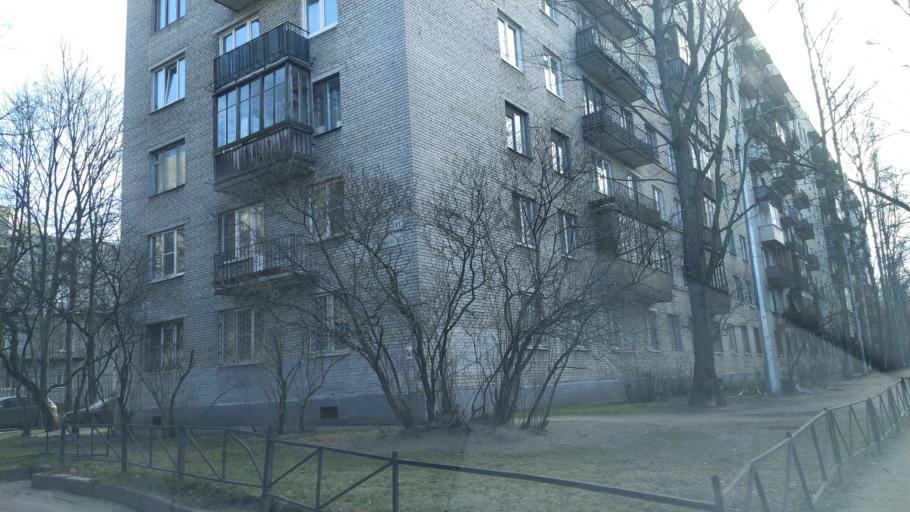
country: RU
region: Leningrad
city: Akademicheskoe
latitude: 60.0074
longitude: 30.3990
